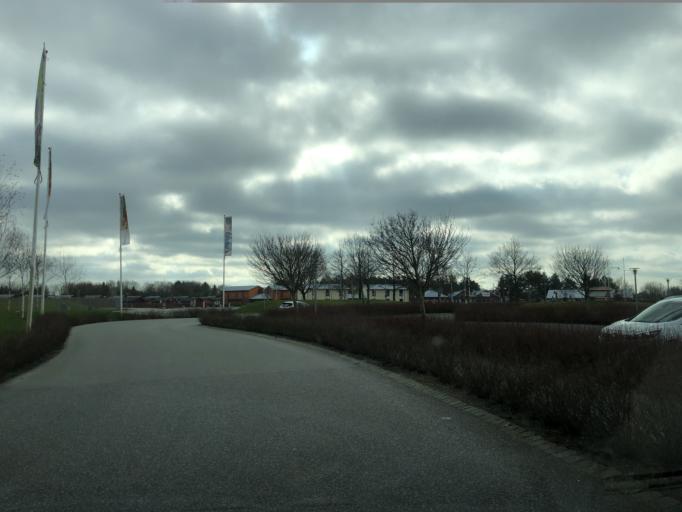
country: DK
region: South Denmark
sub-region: Billund Kommune
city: Billund
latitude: 55.7329
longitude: 9.1364
